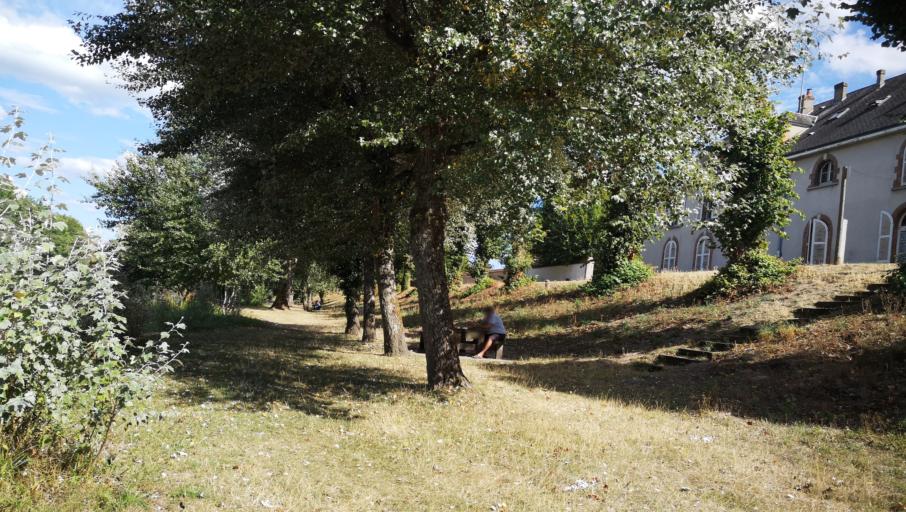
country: FR
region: Centre
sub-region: Departement du Loiret
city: Sully-sur-Loire
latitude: 47.7667
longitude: 2.3782
